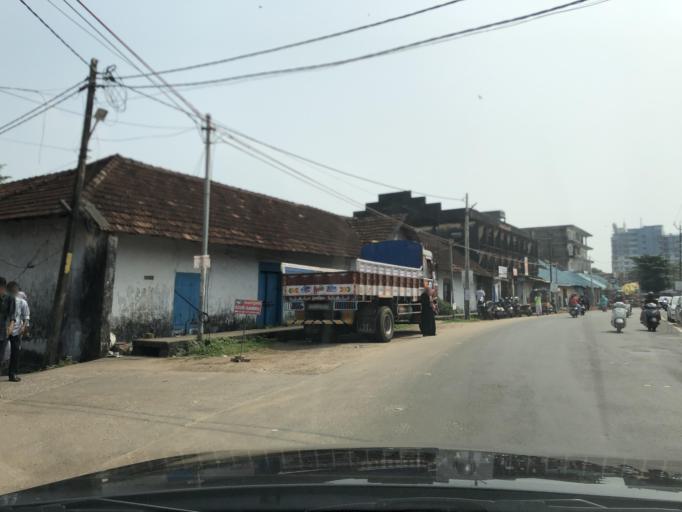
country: IN
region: Kerala
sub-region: Kozhikode
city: Kozhikode
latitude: 11.2499
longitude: 75.7724
